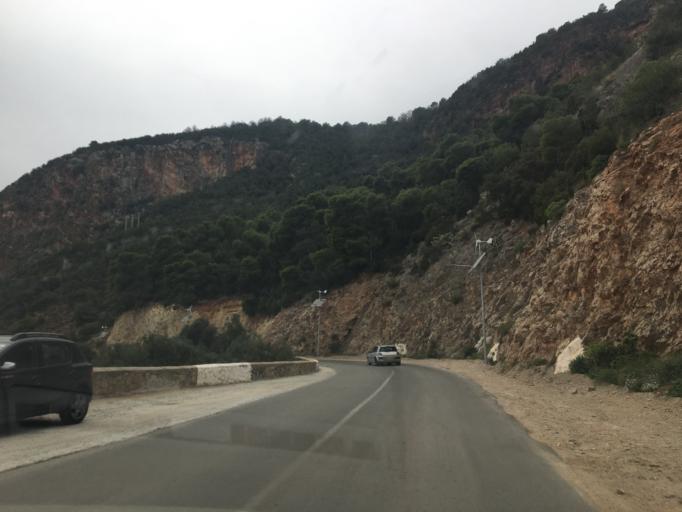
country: DZ
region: Tipaza
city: Tipasa
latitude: 36.6173
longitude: 2.4052
